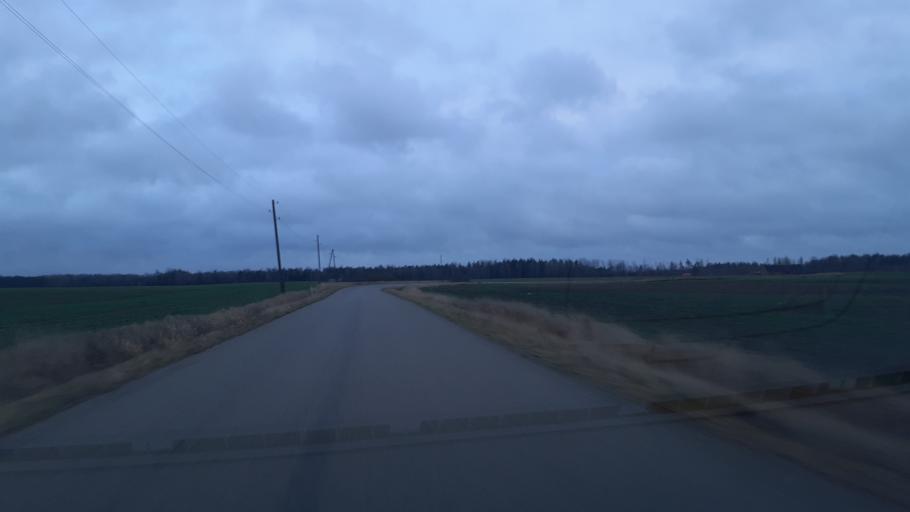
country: LV
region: Kuldigas Rajons
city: Kuldiga
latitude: 57.0270
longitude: 22.1661
